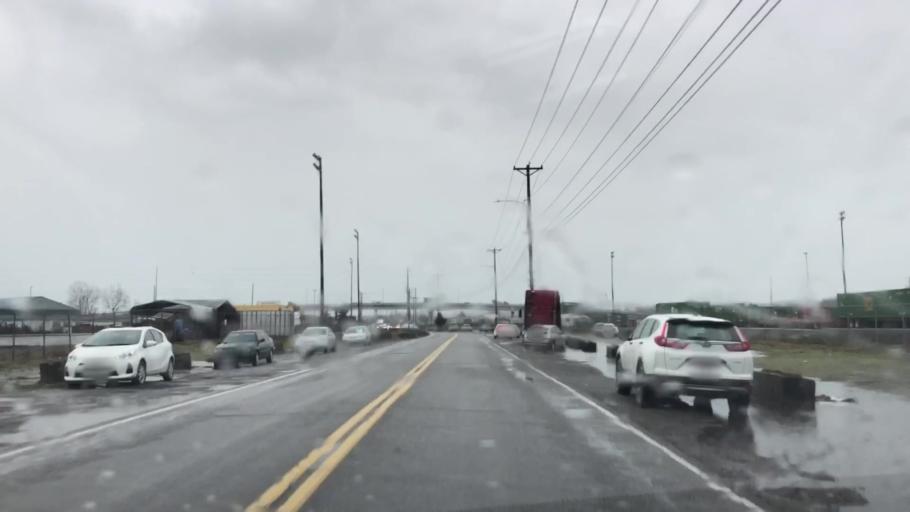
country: US
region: Washington
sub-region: Pierce County
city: Tacoma
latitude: 47.2592
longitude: -122.4087
